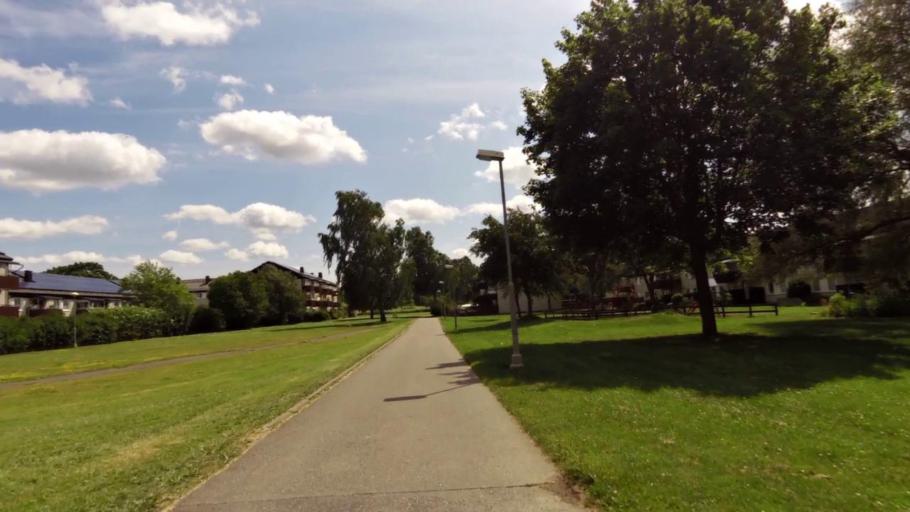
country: SE
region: OEstergoetland
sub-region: Linkopings Kommun
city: Linkoping
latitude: 58.4238
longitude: 15.5785
